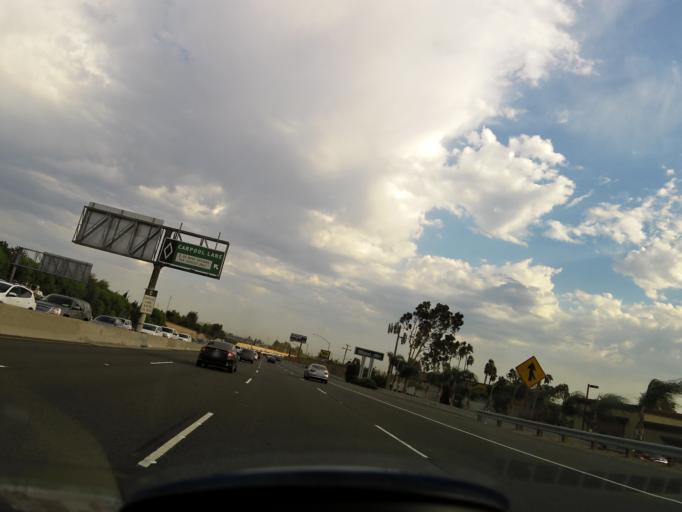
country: US
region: California
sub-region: Orange County
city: Villa Park
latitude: 33.8318
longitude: -117.8351
